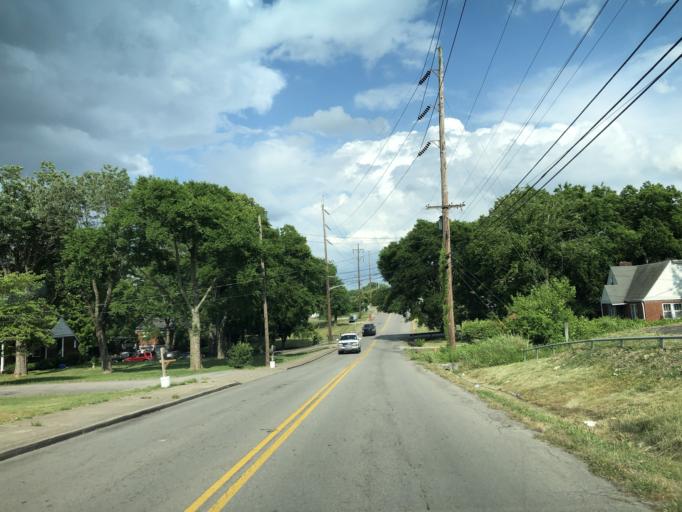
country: US
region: Tennessee
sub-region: Davidson County
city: Goodlettsville
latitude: 36.2733
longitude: -86.7074
